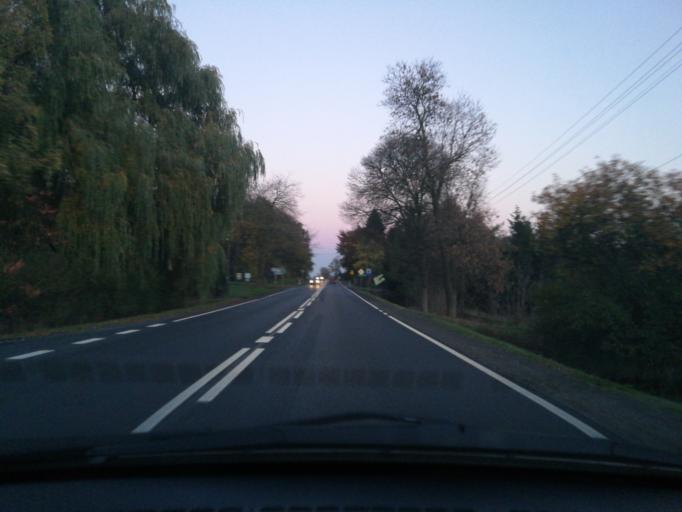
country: PL
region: Lodz Voivodeship
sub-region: Powiat brzezinski
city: Brzeziny
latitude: 51.8043
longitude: 19.6940
